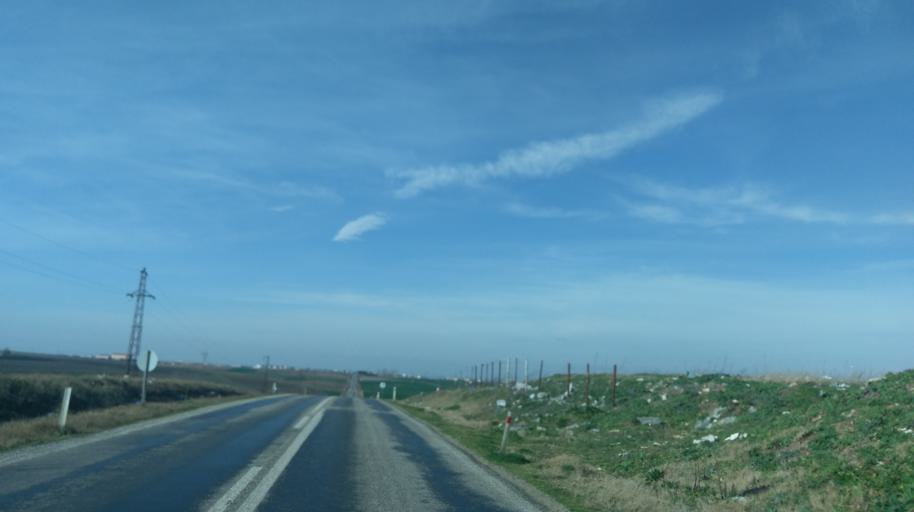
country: TR
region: Edirne
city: Uzun Keupru
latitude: 41.2739
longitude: 26.7346
